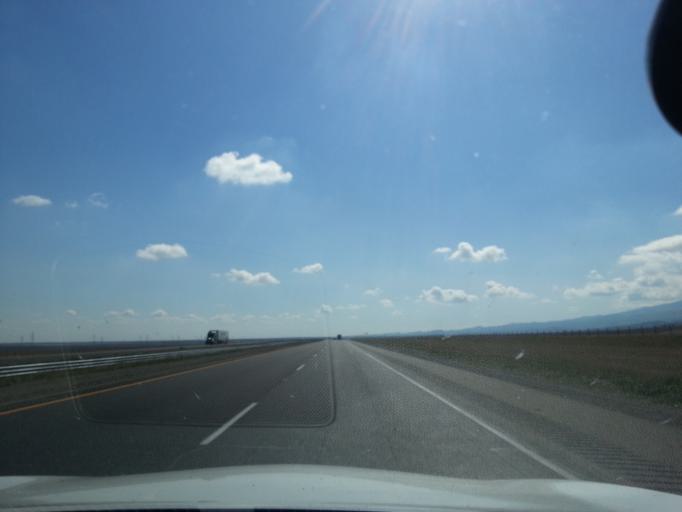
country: US
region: California
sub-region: Fresno County
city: San Joaquin
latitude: 36.4650
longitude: -120.4215
